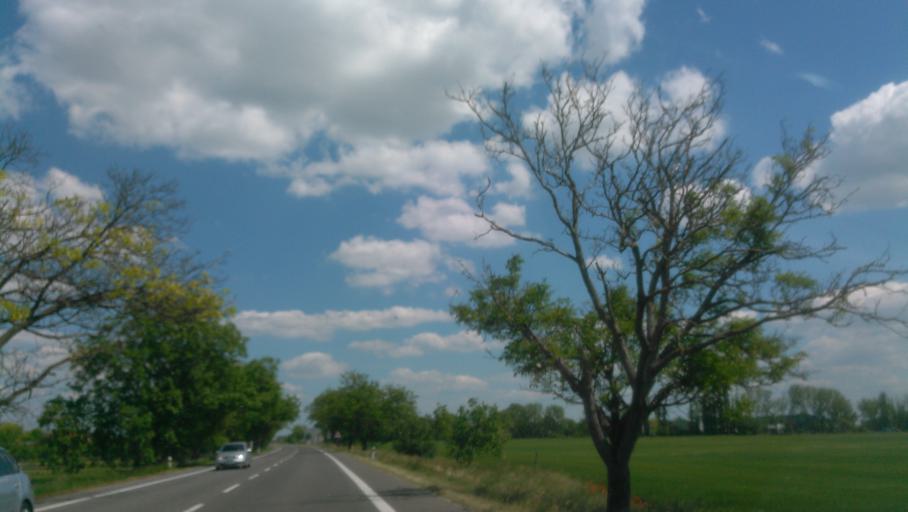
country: SK
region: Trnavsky
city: Samorin
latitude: 47.9987
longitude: 17.4389
